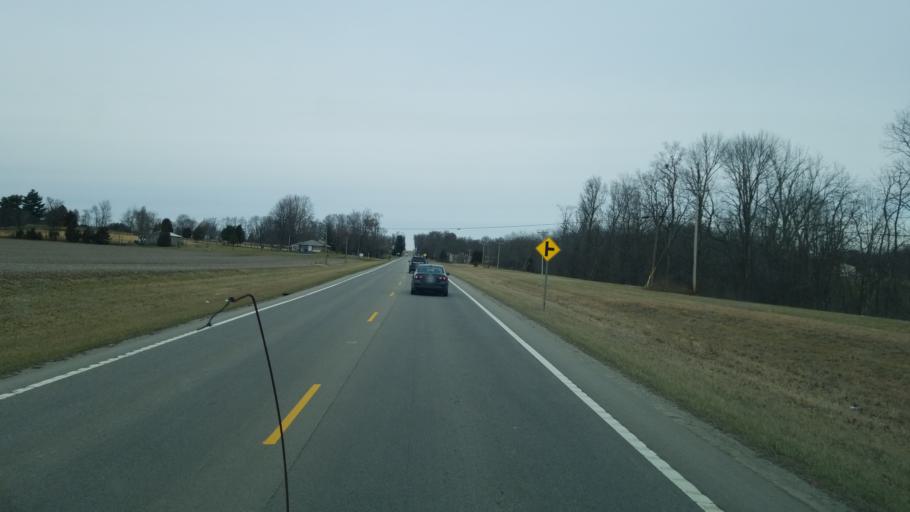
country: US
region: Ohio
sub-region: Highland County
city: Hillsboro
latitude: 39.1281
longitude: -83.6708
